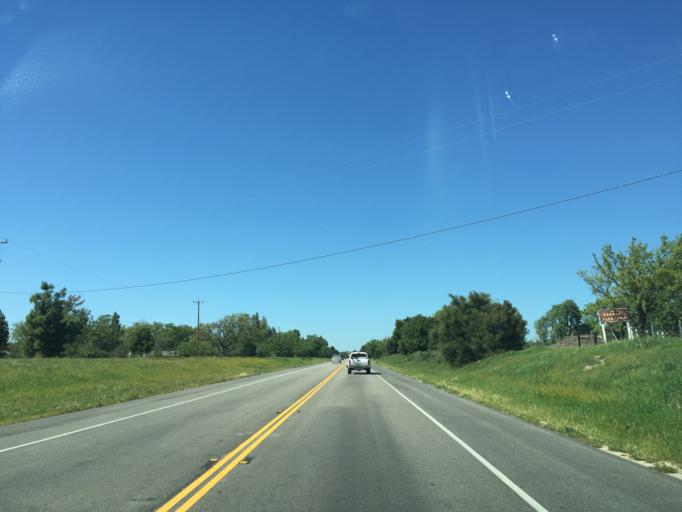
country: US
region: California
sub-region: Santa Barbara County
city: Los Olivos
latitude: 34.6536
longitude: -120.0978
